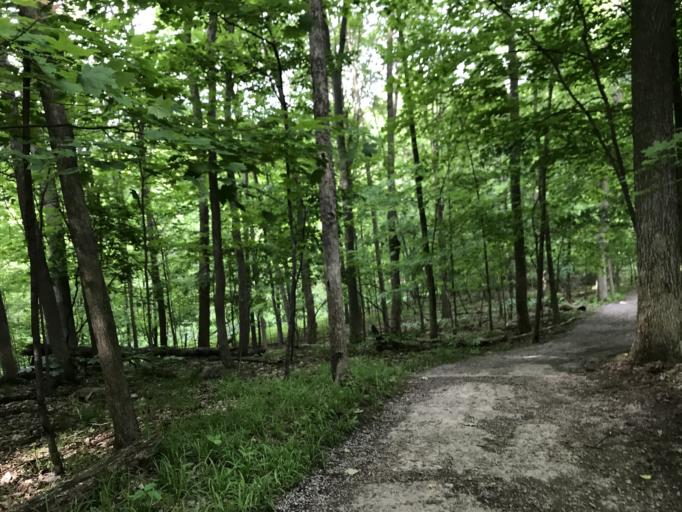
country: US
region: Michigan
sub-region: Oakland County
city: Farmington Hills
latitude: 42.4771
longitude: -83.3889
